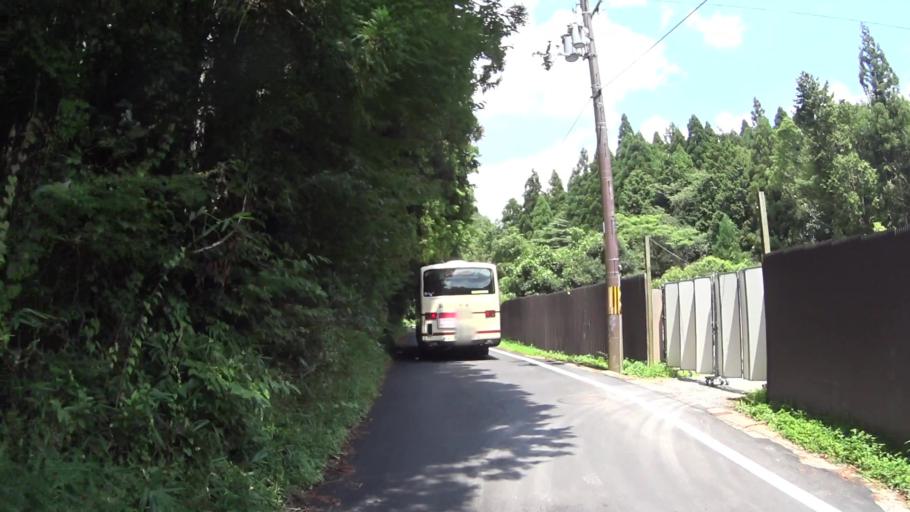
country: JP
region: Shiga Prefecture
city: Kitahama
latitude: 35.1292
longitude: 135.8313
